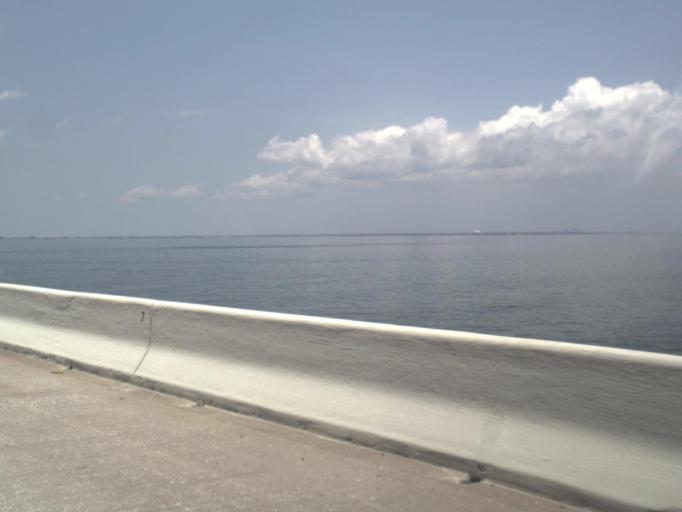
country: US
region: Florida
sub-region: Manatee County
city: Memphis
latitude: 27.5935
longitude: -82.6314
